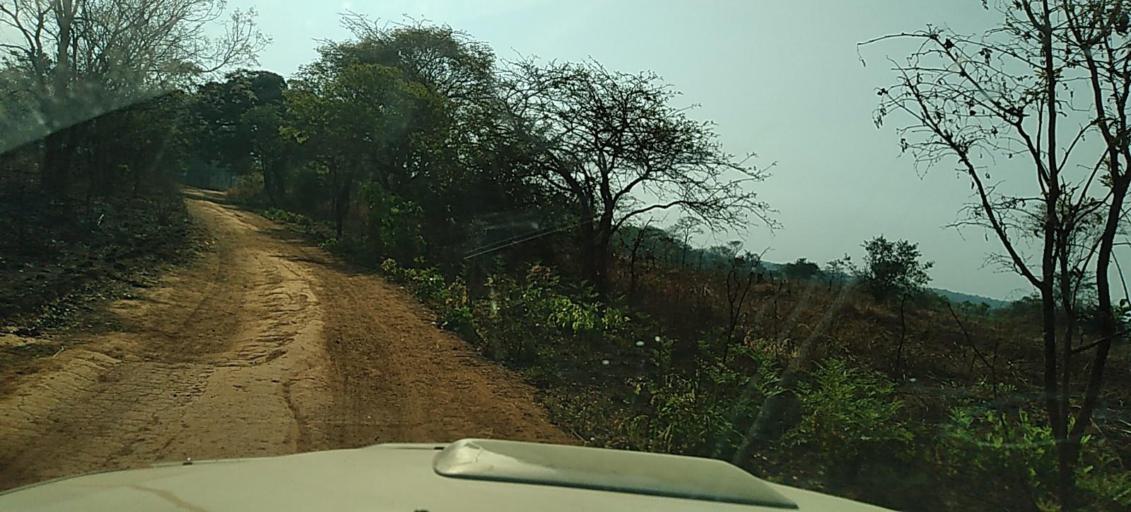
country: ZM
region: North-Western
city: Kasempa
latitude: -13.1854
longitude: 25.9586
